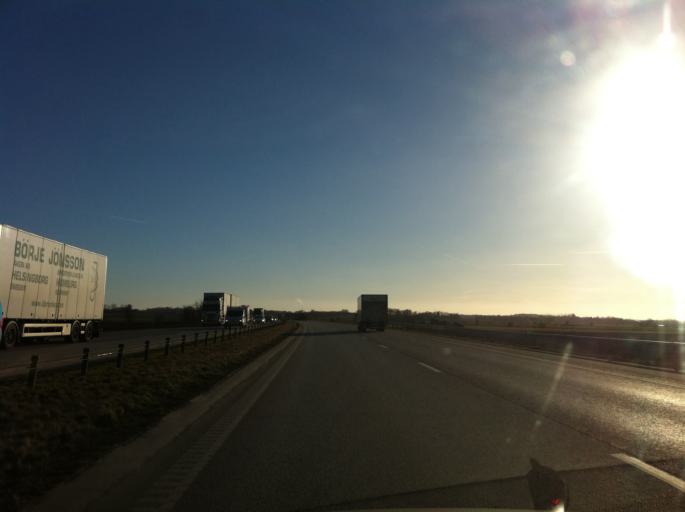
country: SE
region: Skane
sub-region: Angelholms Kommun
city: Strovelstorp
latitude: 56.1200
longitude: 12.8177
